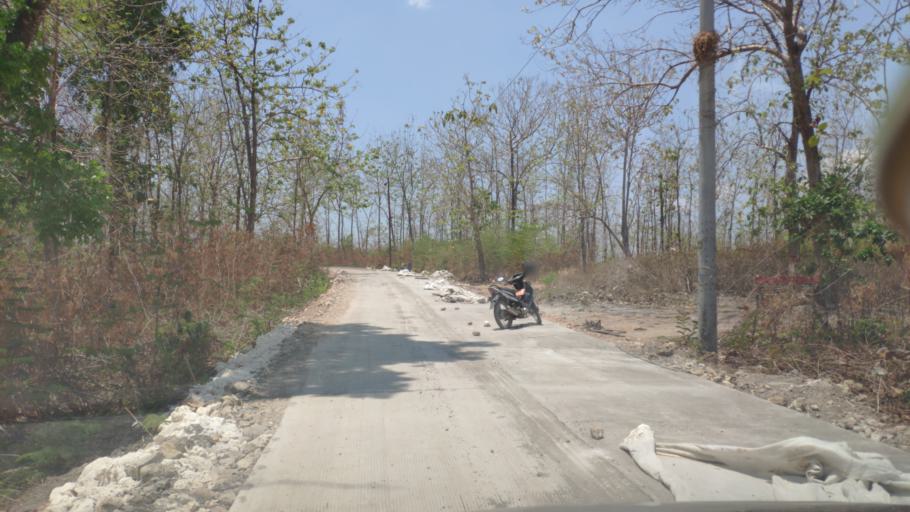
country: ID
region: Central Java
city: Randublatung
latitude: -7.2670
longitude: 111.3785
